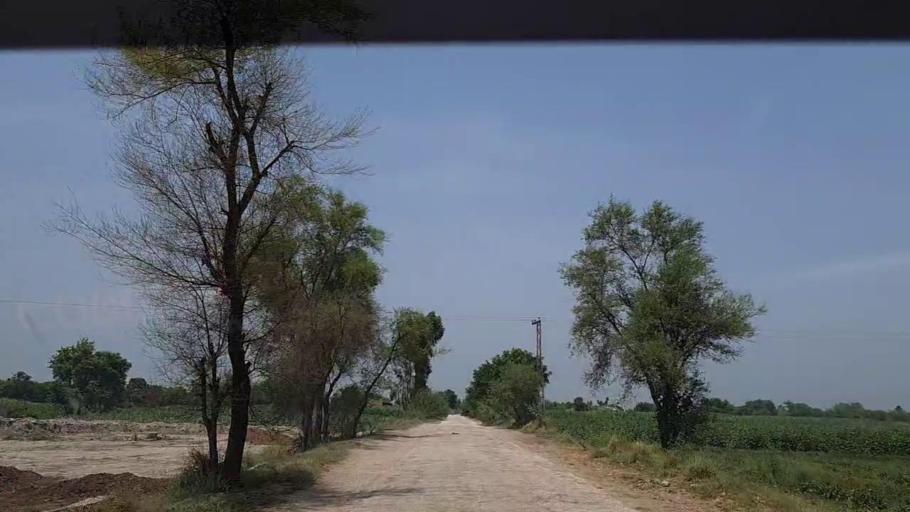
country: PK
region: Sindh
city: Ghotki
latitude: 28.0159
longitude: 69.3550
